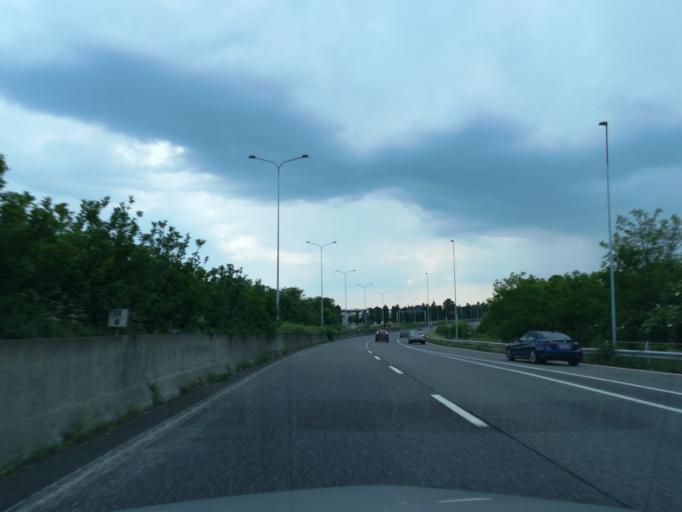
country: IT
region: Lombardy
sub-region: Provincia di Bergamo
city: Orio al Serio
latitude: 45.6760
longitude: 9.6832
